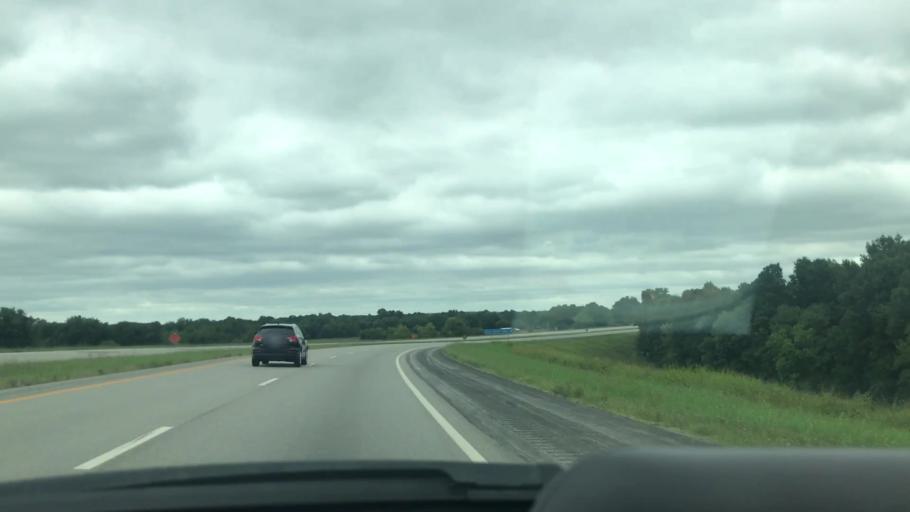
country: US
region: Oklahoma
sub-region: Mayes County
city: Pryor
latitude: 36.3743
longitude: -95.2957
